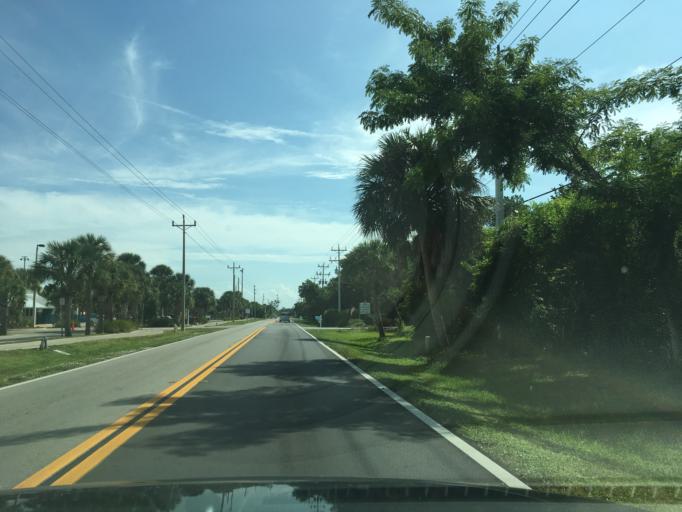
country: US
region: Florida
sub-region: Lee County
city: Saint James City
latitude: 26.4466
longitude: -82.1169
